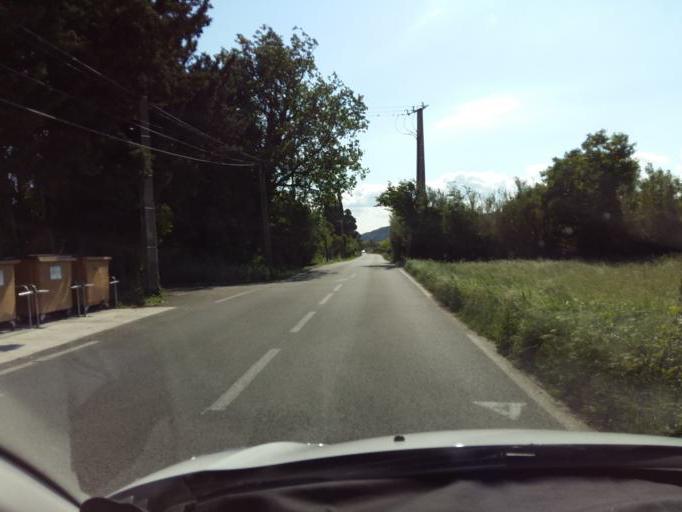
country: FR
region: Provence-Alpes-Cote d'Azur
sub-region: Departement du Vaucluse
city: Cavaillon
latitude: 43.8463
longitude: 5.0571
